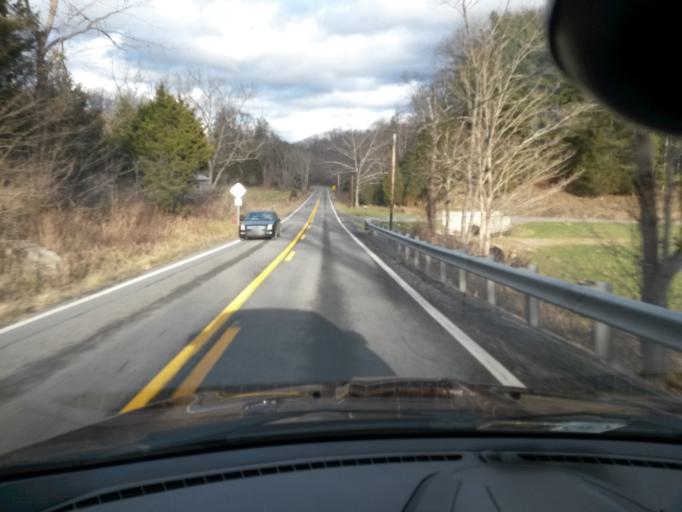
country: US
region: West Virginia
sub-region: Monroe County
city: Union
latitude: 37.4851
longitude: -80.6108
